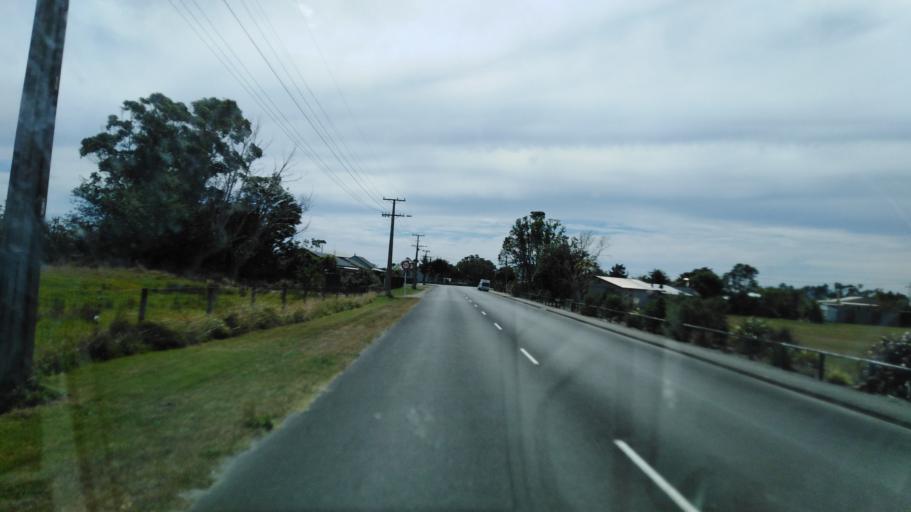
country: NZ
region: West Coast
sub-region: Buller District
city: Westport
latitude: -41.7424
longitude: 171.6031
